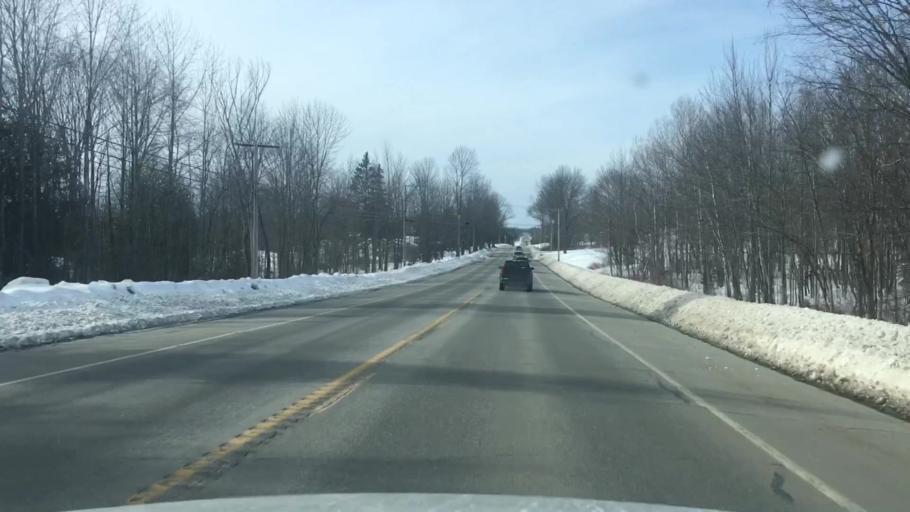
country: US
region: Maine
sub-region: Penobscot County
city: Kenduskeag
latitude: 44.9725
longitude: -68.9800
